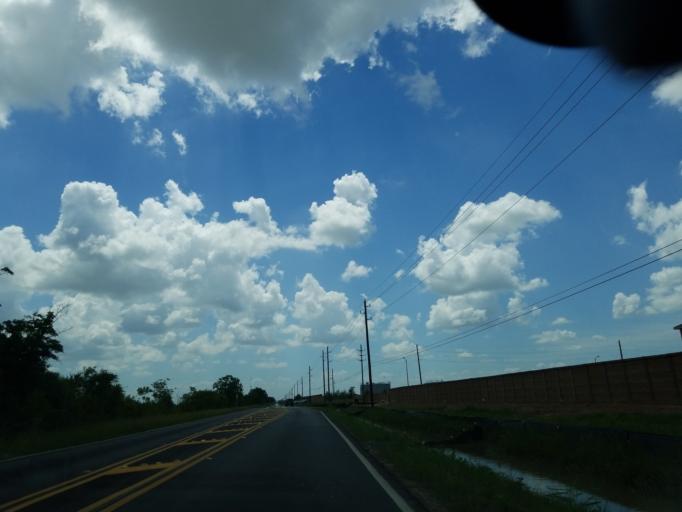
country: US
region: Texas
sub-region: Harris County
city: Katy
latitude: 29.8460
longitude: -95.7926
